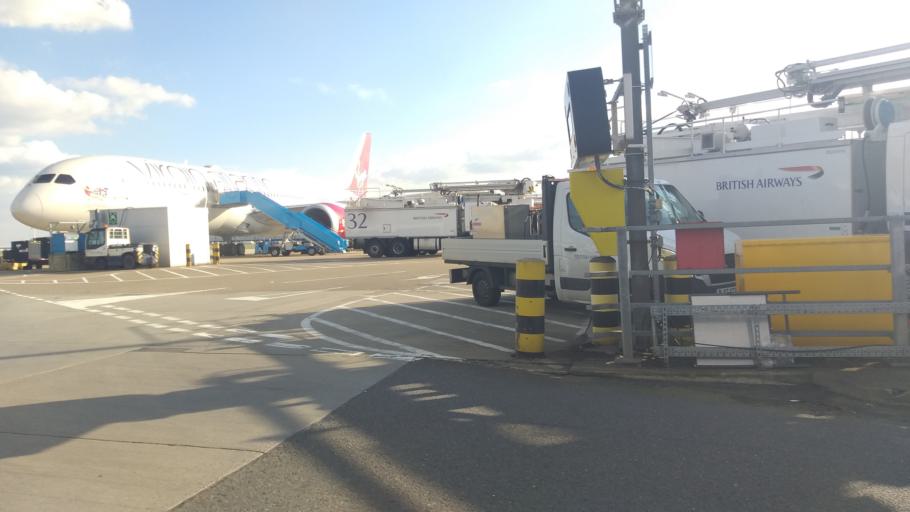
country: GB
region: England
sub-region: Greater London
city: West Drayton
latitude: 51.4690
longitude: -0.4715
